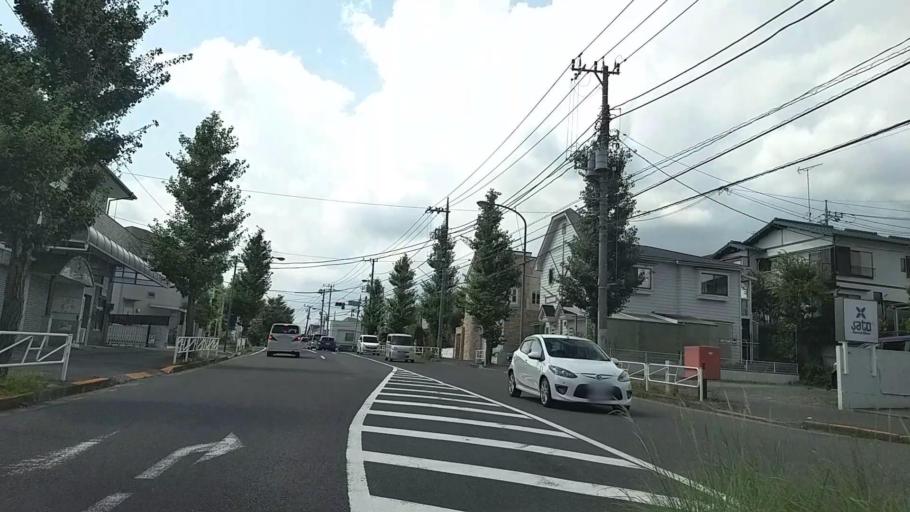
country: JP
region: Tokyo
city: Hachioji
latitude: 35.6476
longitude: 139.3105
